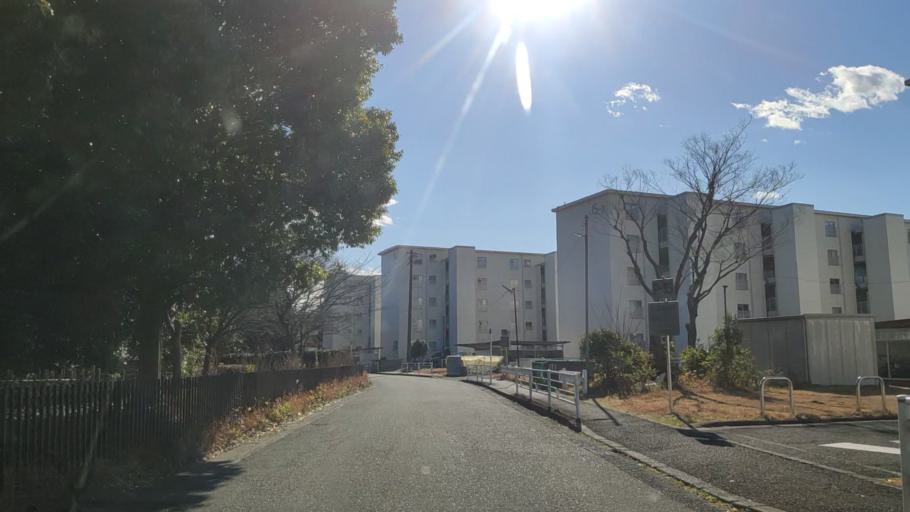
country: JP
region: Kanagawa
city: Minami-rinkan
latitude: 35.5020
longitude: 139.5314
